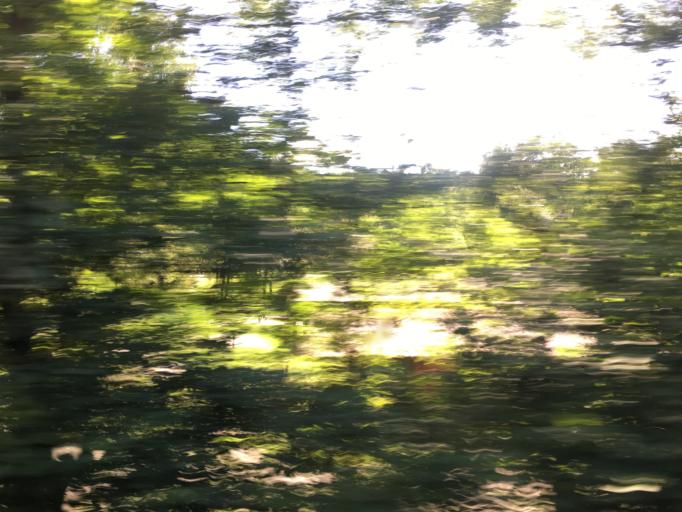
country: DE
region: Hesse
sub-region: Regierungsbezirk Darmstadt
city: Wehrheim
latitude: 50.2848
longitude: 8.5829
